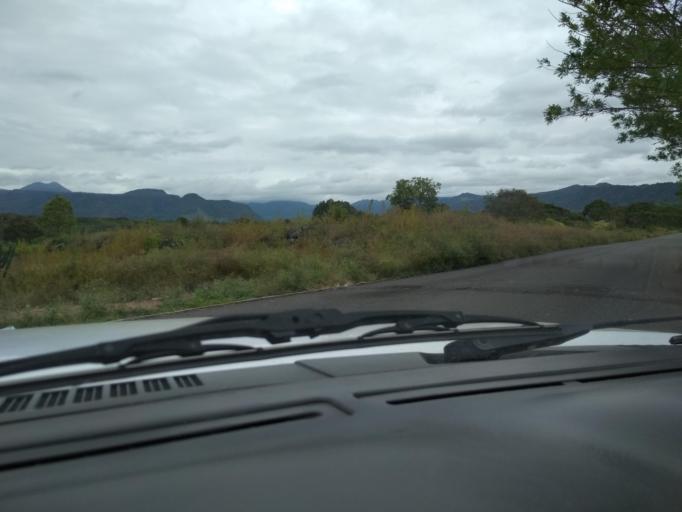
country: MX
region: Veracruz
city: Alto Lucero
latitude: 19.5976
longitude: -96.7810
